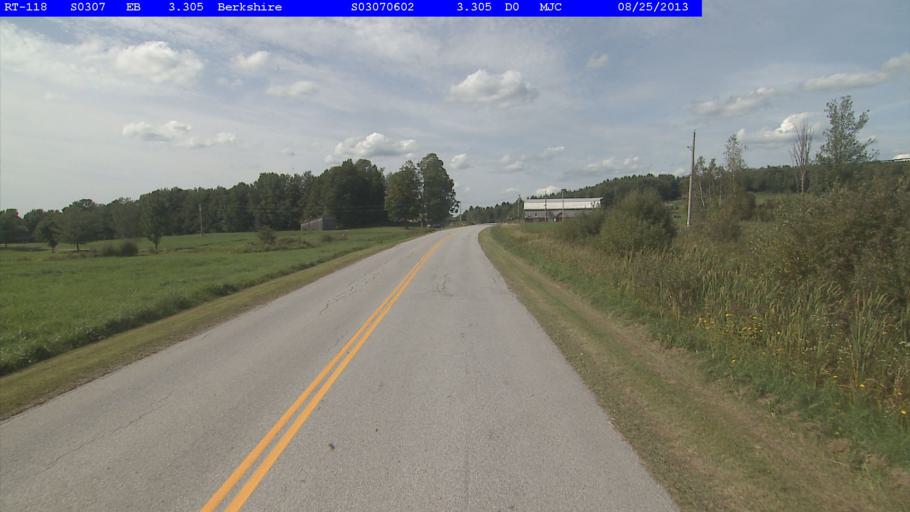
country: US
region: Vermont
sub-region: Franklin County
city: Enosburg Falls
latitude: 44.9630
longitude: -72.7587
